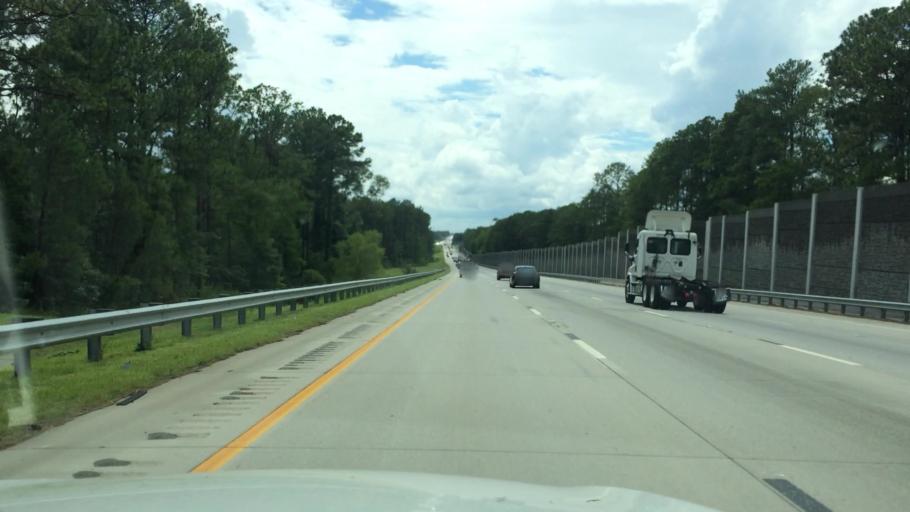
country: US
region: South Carolina
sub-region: Richland County
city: Woodfield
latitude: 34.0924
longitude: -80.8627
